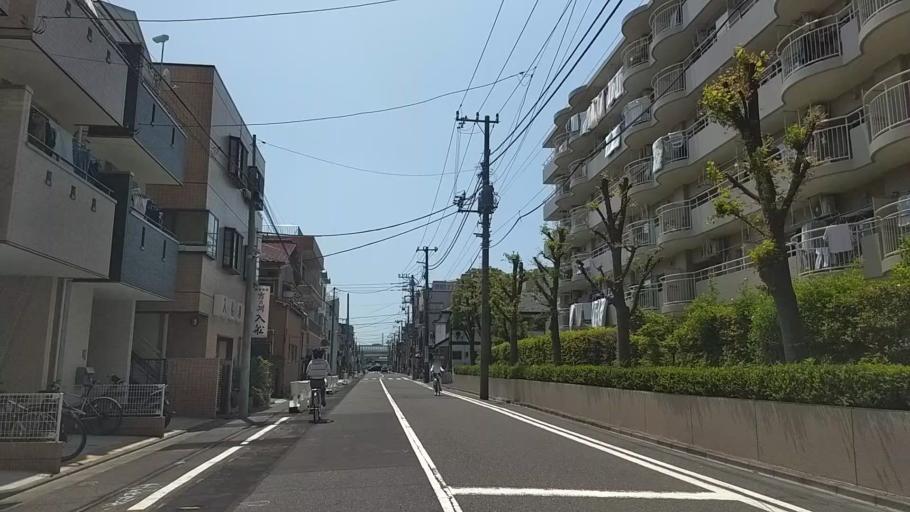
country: JP
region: Kanagawa
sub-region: Kawasaki-shi
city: Kawasaki
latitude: 35.5058
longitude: 139.6985
